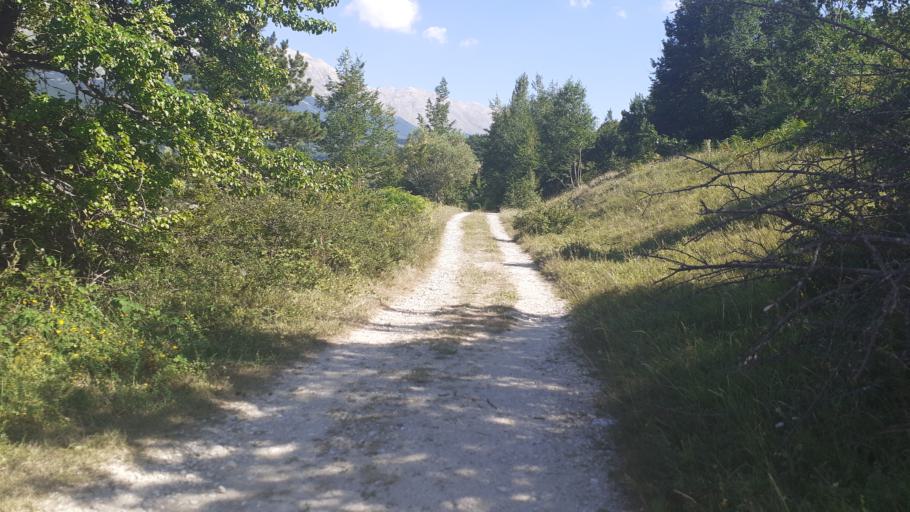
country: IT
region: Abruzzo
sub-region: Provincia di Pescara
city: Sant'Eufemia a Maiella
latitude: 42.1030
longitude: 14.0090
